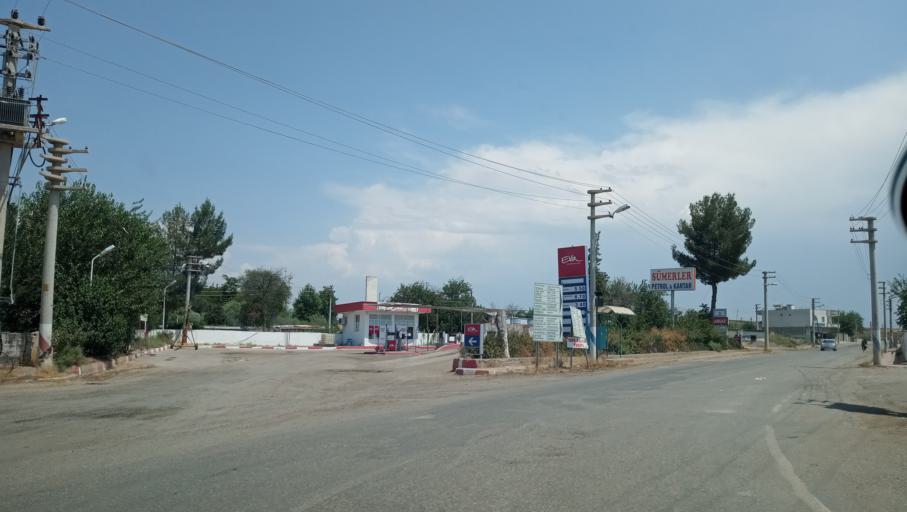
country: TR
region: Diyarbakir
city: Tepe
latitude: 37.7930
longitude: 40.7778
